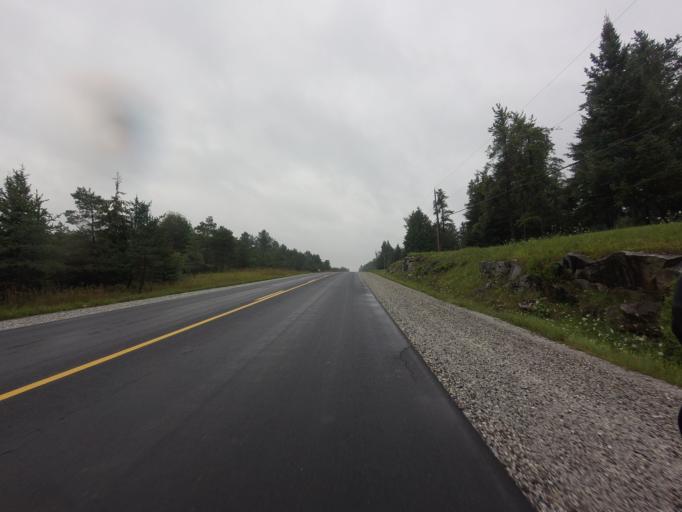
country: CA
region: Ontario
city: Perth
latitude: 45.0899
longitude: -76.4550
